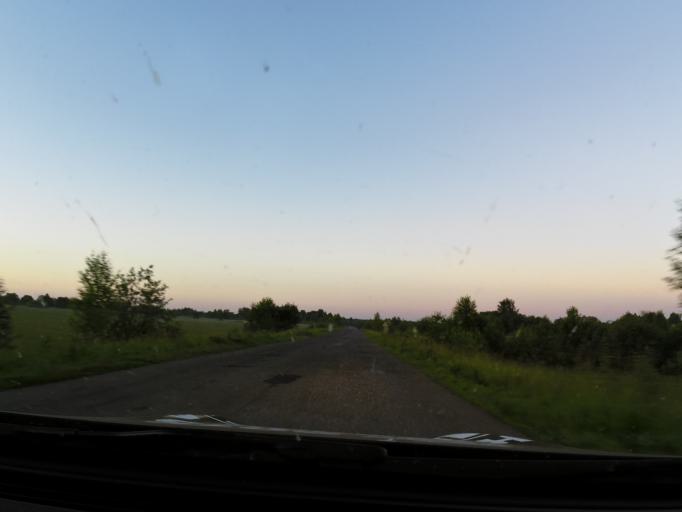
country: RU
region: Kostroma
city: Buy
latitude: 58.3549
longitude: 41.1863
